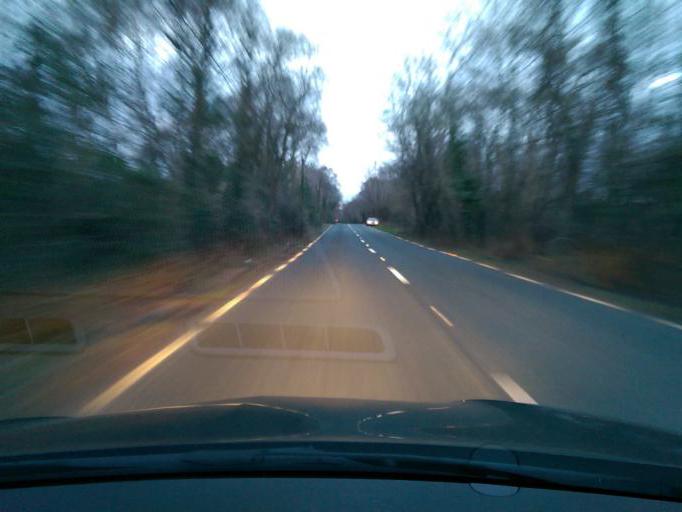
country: IE
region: Connaught
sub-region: County Galway
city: Portumna
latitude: 53.1470
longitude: -8.2586
